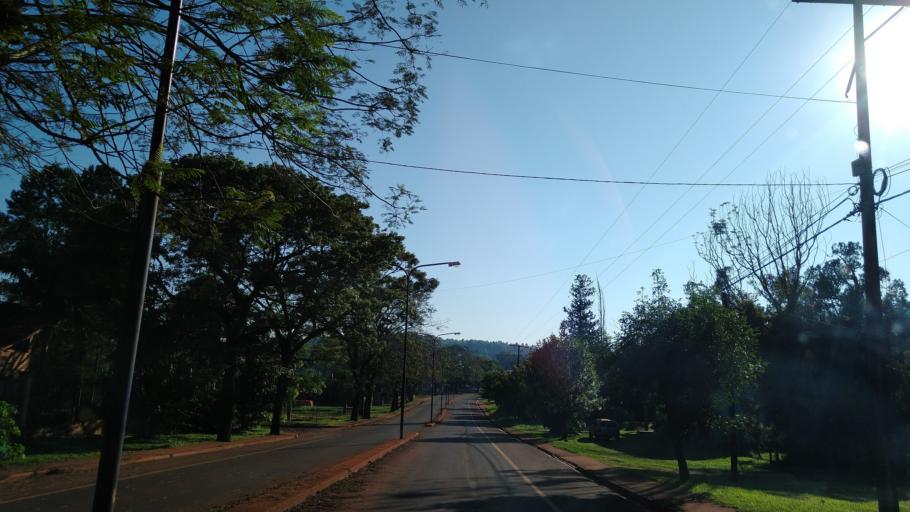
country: AR
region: Misiones
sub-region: Departamento de Montecarlo
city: Montecarlo
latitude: -26.5736
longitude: -54.7440
